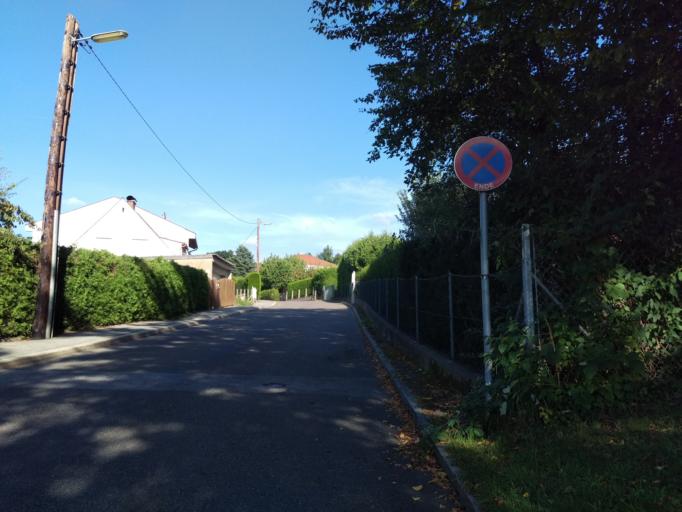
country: AT
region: Styria
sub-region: Graz Stadt
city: Graz
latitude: 47.0690
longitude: 15.4765
